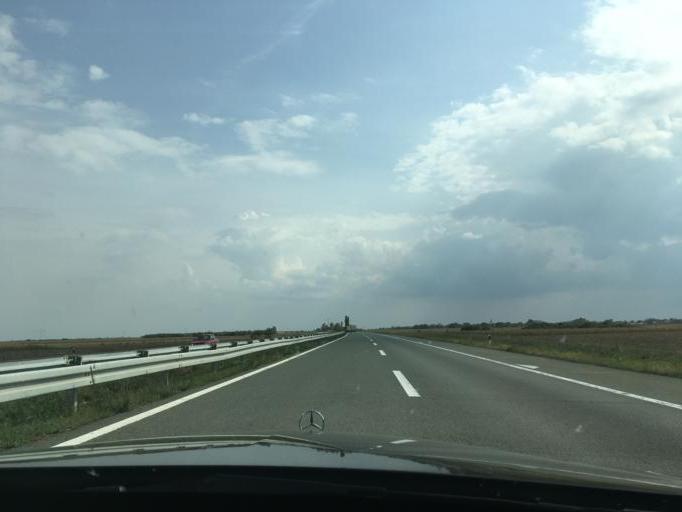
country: RS
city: Sasinci
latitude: 44.9829
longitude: 19.7214
